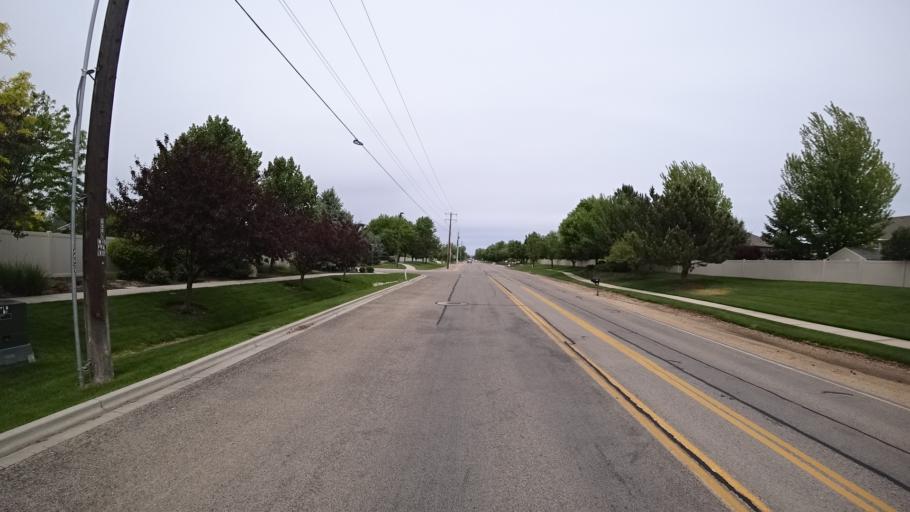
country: US
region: Idaho
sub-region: Ada County
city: Meridian
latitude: 43.5692
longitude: -116.3746
